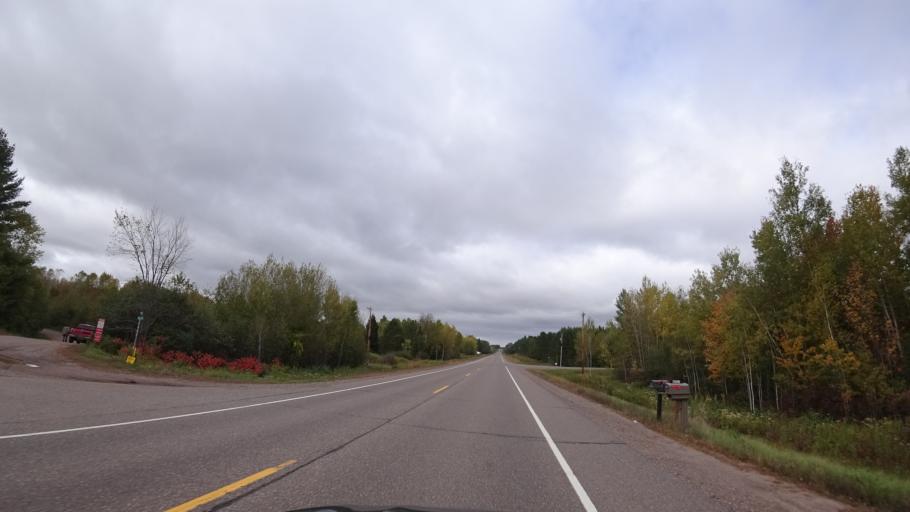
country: US
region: Wisconsin
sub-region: Rusk County
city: Ladysmith
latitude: 45.5223
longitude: -91.1115
